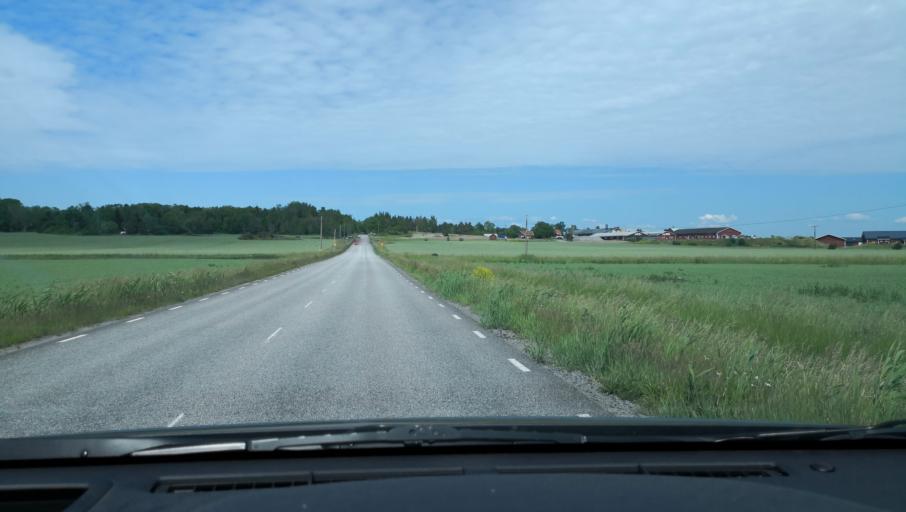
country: SE
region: Stockholm
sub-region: Sigtuna Kommun
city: Sigtuna
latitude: 59.6742
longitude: 17.6973
